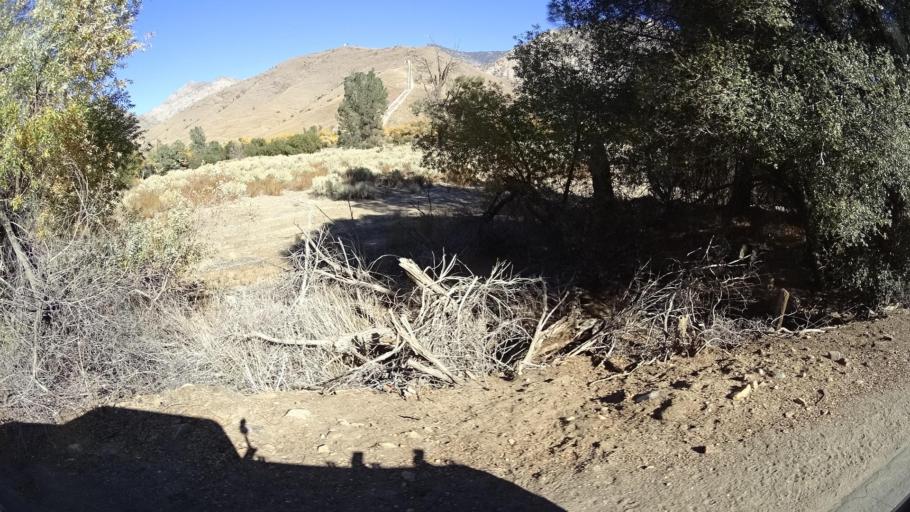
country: US
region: California
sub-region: Kern County
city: Kernville
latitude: 35.7722
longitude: -118.4402
